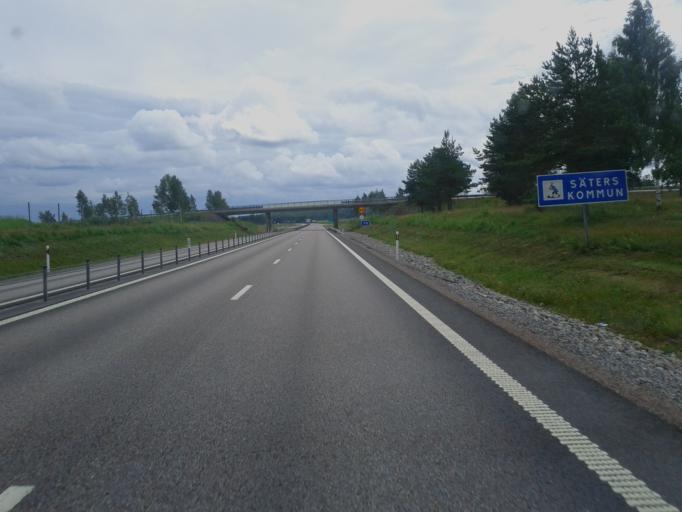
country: SE
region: Dalarna
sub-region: Borlange Kommun
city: Ornas
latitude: 60.4191
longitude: 15.5542
